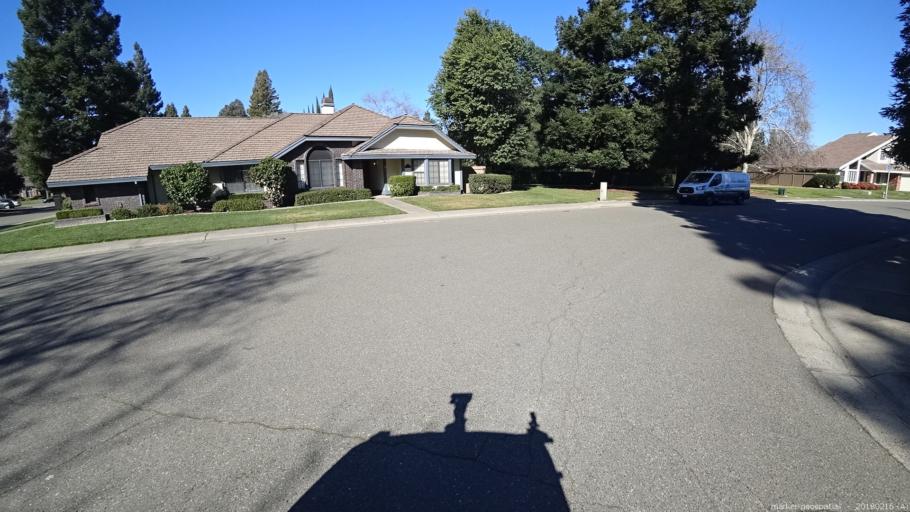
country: US
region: California
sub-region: Sacramento County
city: Gold River
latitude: 38.6205
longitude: -121.2486
